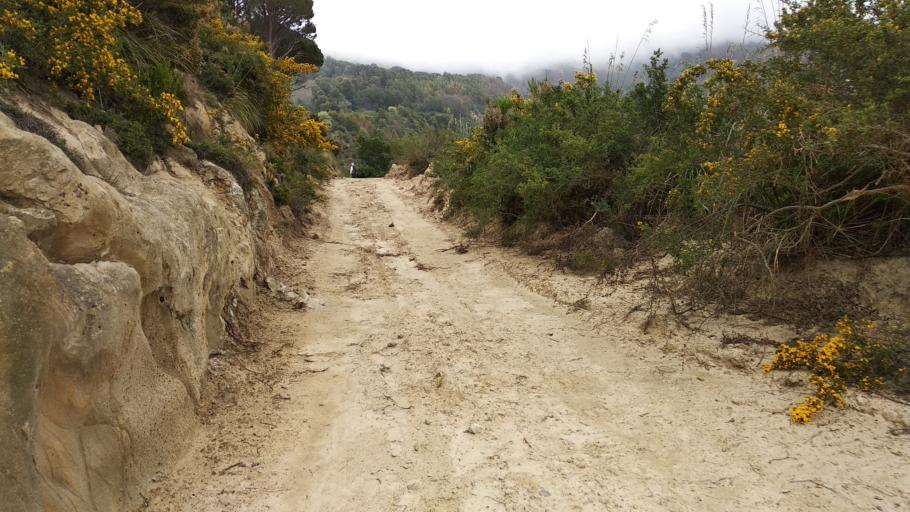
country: IT
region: Sicily
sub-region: Messina
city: Saponara
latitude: 38.2092
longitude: 15.4813
